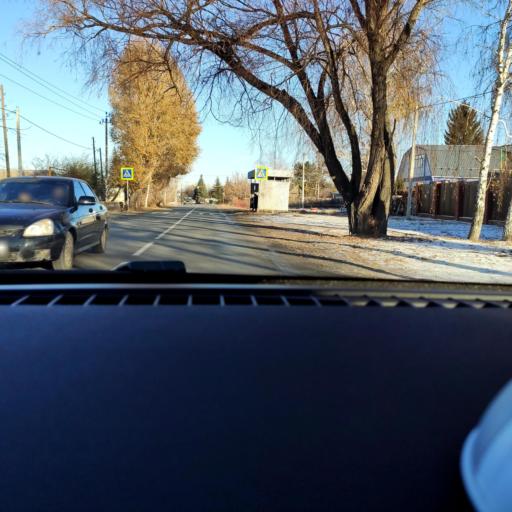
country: RU
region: Samara
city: Novokuybyshevsk
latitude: 53.1210
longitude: 49.8983
